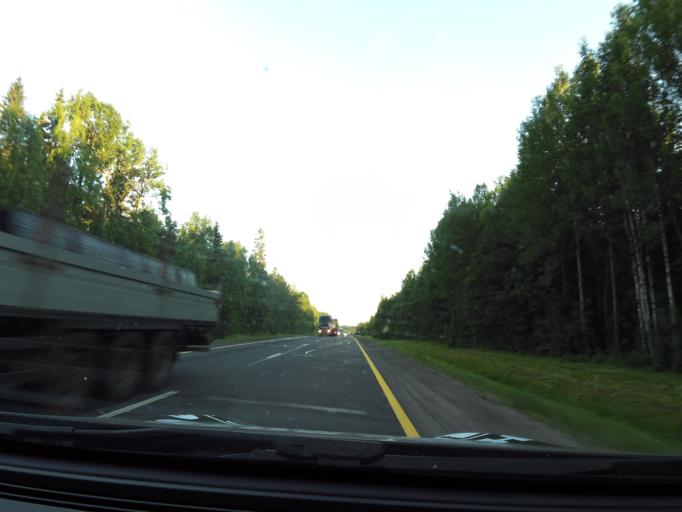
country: RU
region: Jaroslavl
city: Prechistoye
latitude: 58.5166
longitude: 40.3466
